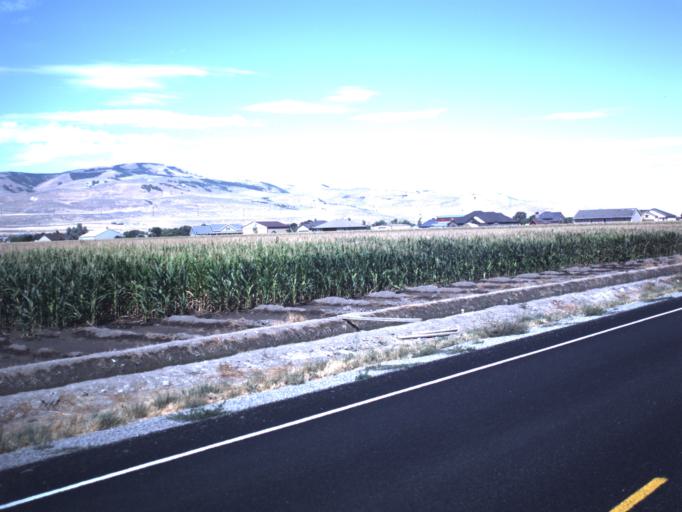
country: US
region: Utah
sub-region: Box Elder County
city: Garland
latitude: 41.7322
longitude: -112.1431
